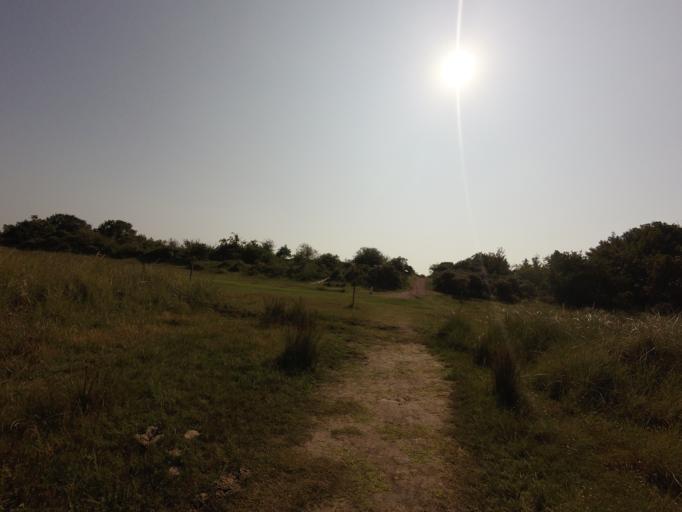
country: NL
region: Friesland
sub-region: Gemeente Schiermonnikoog
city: Schiermonnikoog
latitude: 53.4879
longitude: 6.2225
